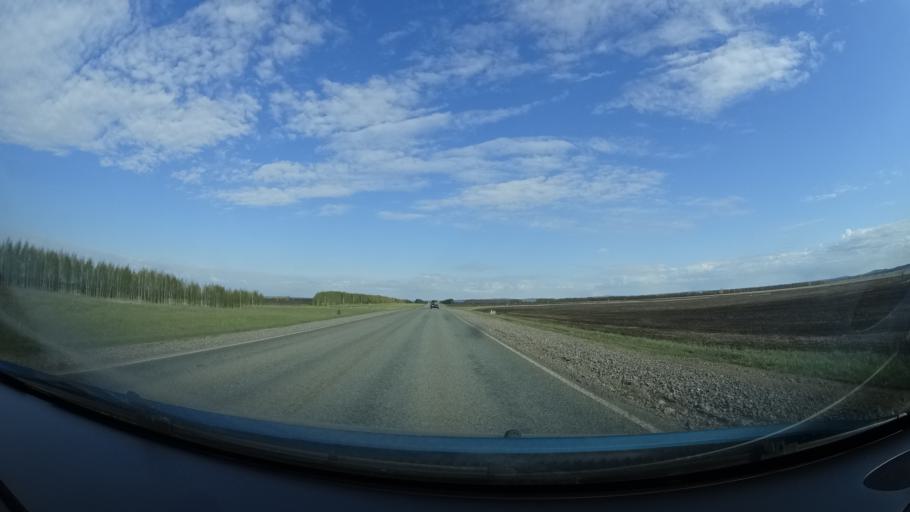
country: RU
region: Bashkortostan
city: Blagoveshchensk
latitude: 55.2083
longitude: 55.8155
